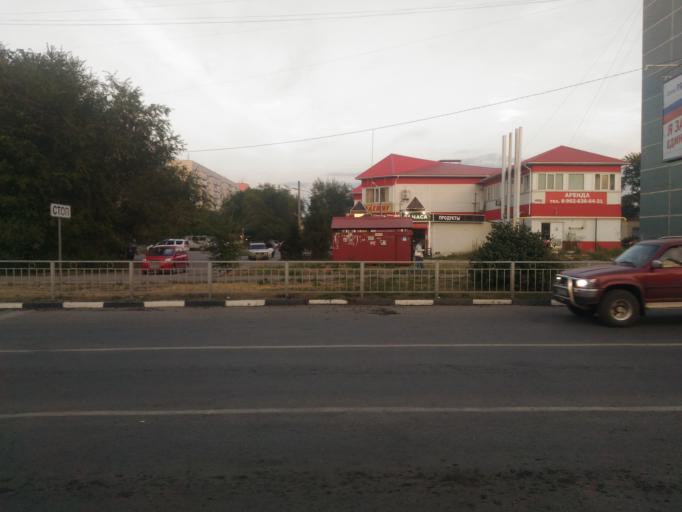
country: RU
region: Ulyanovsk
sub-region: Ulyanovskiy Rayon
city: Ulyanovsk
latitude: 54.2700
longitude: 48.2859
